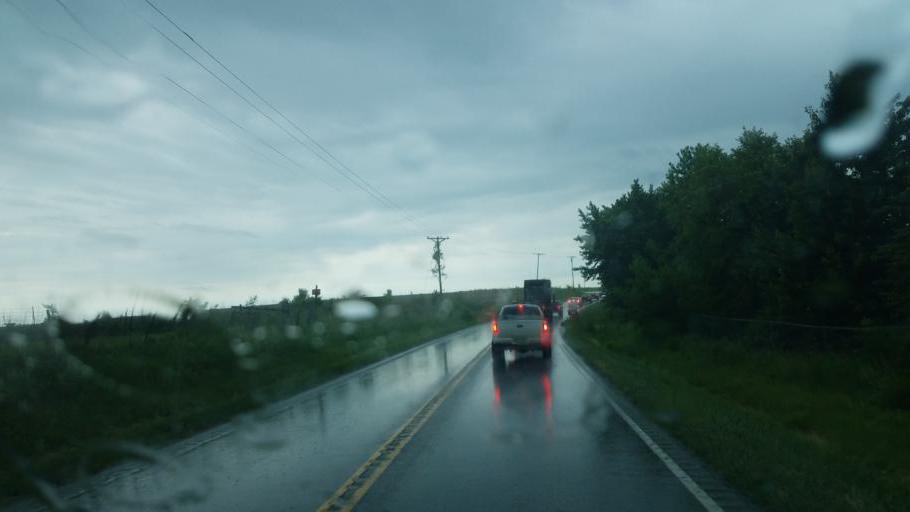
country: US
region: Missouri
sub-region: Cooper County
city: Boonville
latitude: 38.8887
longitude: -92.6534
